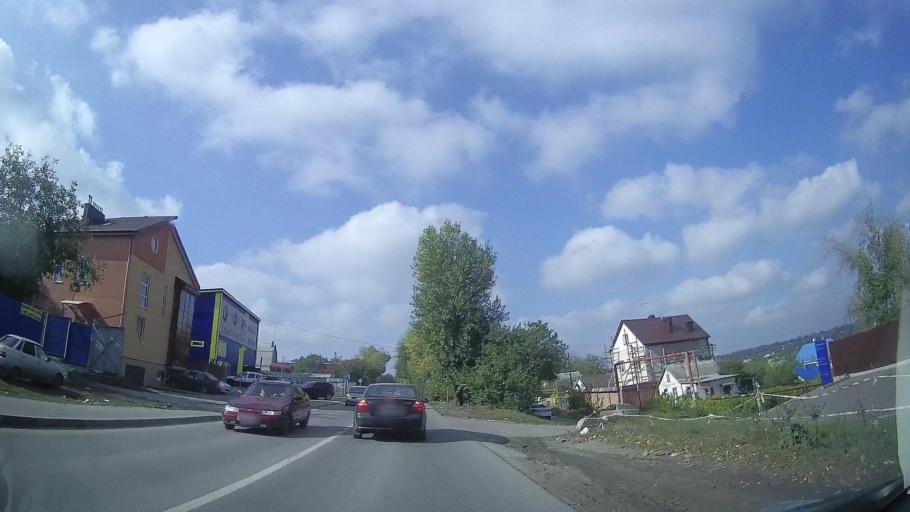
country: RU
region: Rostov
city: Severnyy
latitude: 47.2807
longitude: 39.6835
